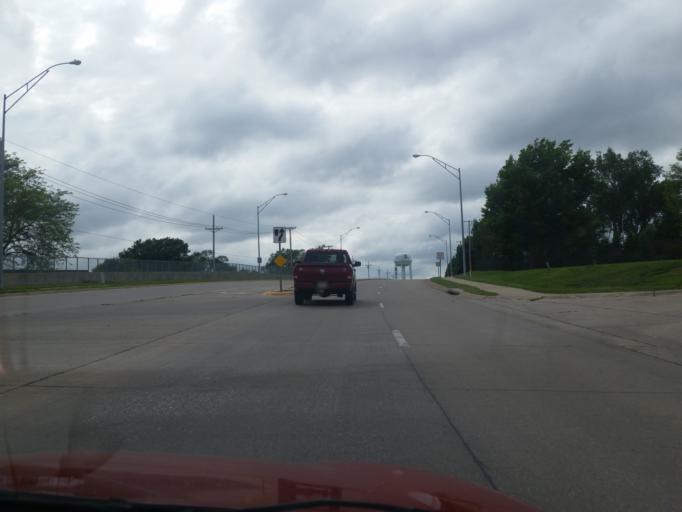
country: US
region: Nebraska
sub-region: Sarpy County
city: Offutt Air Force Base
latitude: 41.1188
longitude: -95.9488
